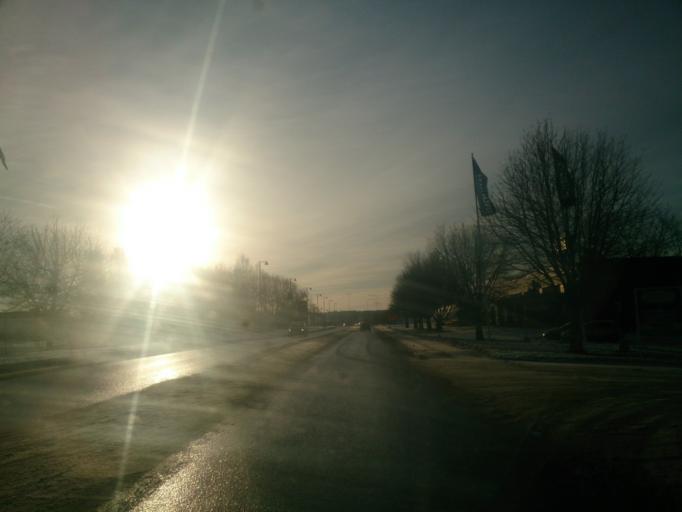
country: SE
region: OEstergoetland
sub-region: Norrkopings Kommun
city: Norrkoping
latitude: 58.6086
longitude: 16.1785
